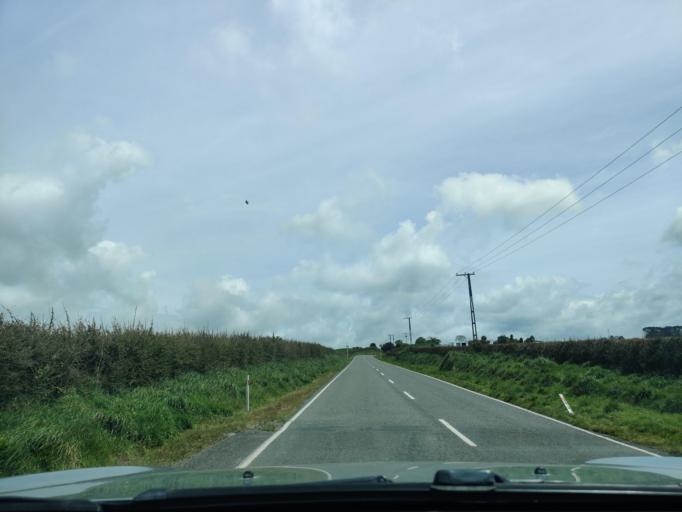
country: NZ
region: Taranaki
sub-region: South Taranaki District
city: Eltham
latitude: -39.3765
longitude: 174.1791
